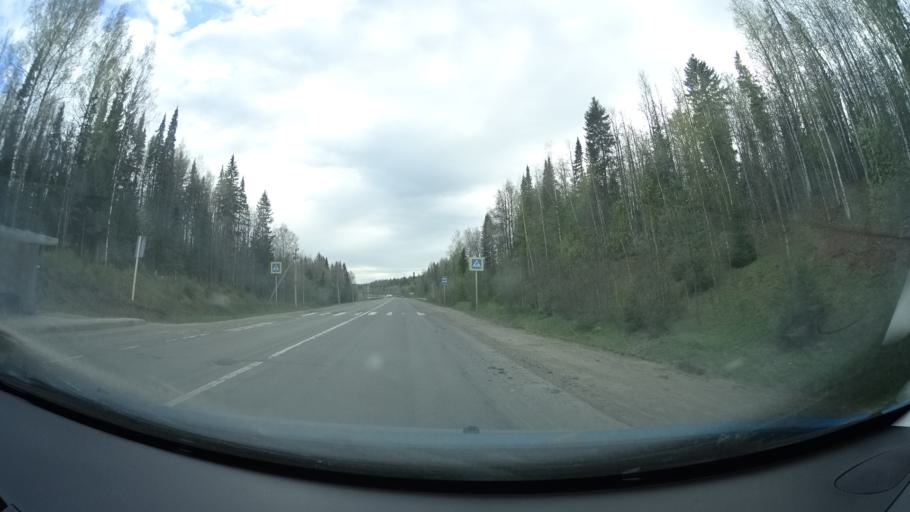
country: RU
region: Perm
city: Kultayevo
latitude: 57.8110
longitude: 55.7904
